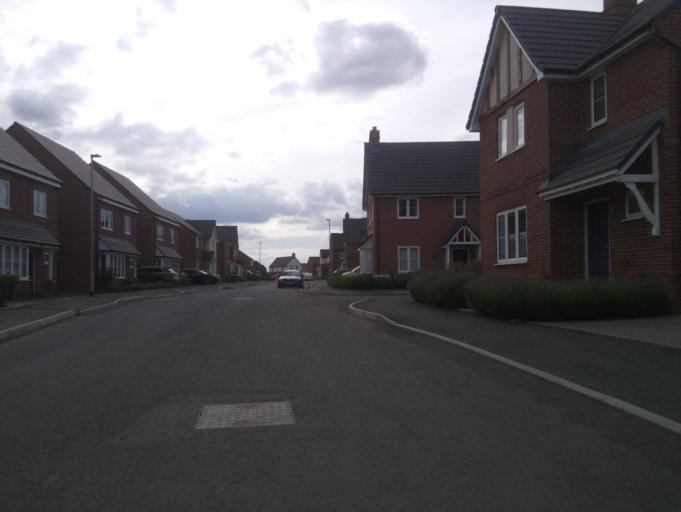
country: GB
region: England
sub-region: Worcestershire
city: Evesham
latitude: 52.0840
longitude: -1.9673
